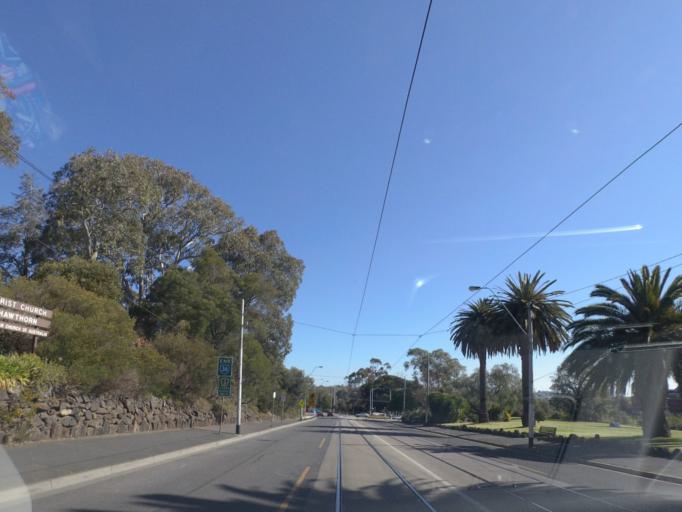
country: AU
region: Victoria
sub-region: Yarra
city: Richmond
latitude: -37.8191
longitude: 145.0176
